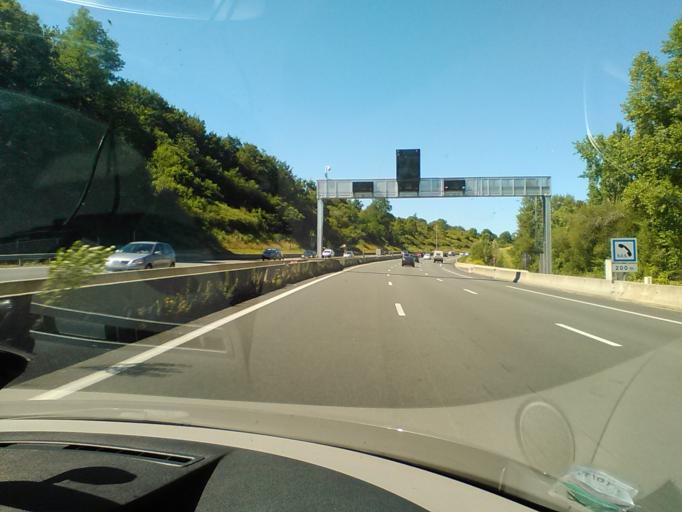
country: FR
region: Aquitaine
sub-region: Departement des Pyrenees-Atlantiques
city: Bayonne
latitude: 43.4718
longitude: -1.4635
